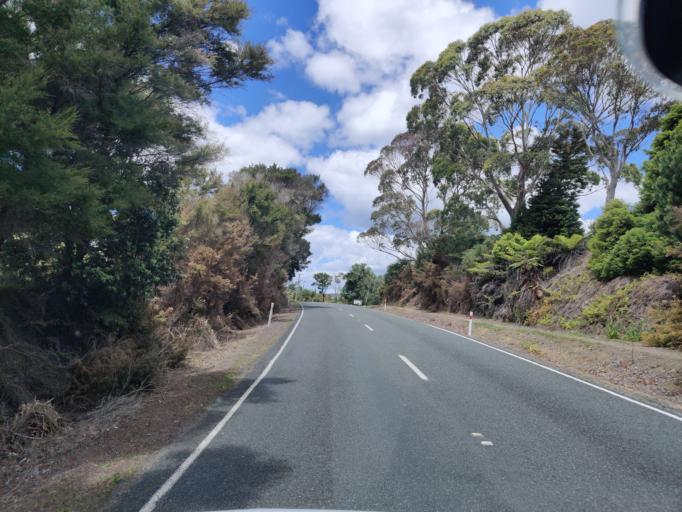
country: NZ
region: Northland
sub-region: Far North District
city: Paihia
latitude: -35.2795
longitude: 174.1409
